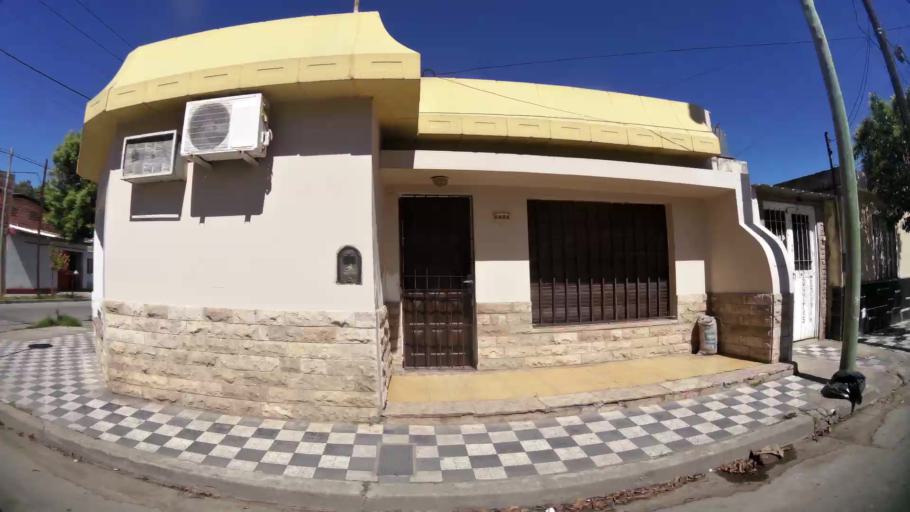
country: AR
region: Cordoba
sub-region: Departamento de Capital
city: Cordoba
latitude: -31.4379
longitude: -64.1357
